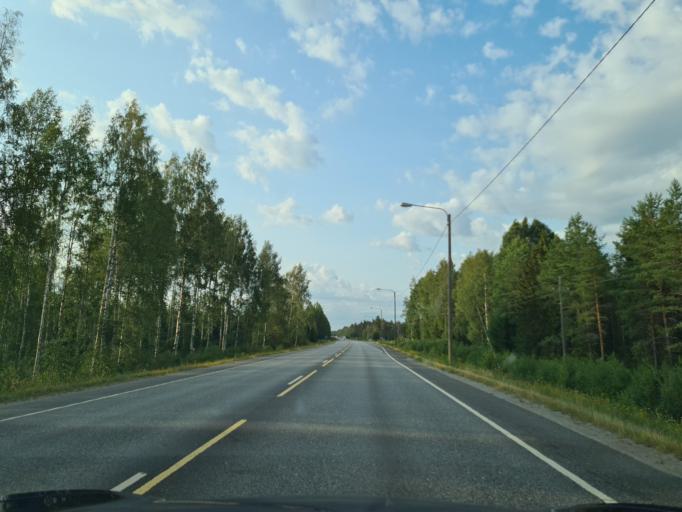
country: FI
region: Southern Ostrobothnia
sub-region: Seinaejoki
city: Lapua
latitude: 63.0046
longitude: 23.0539
